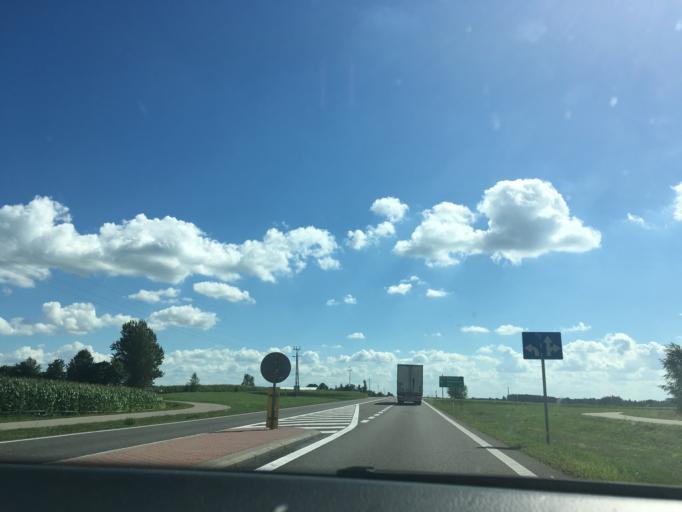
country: PL
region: Podlasie
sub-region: Powiat sokolski
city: Suchowola
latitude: 53.7154
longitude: 23.1025
